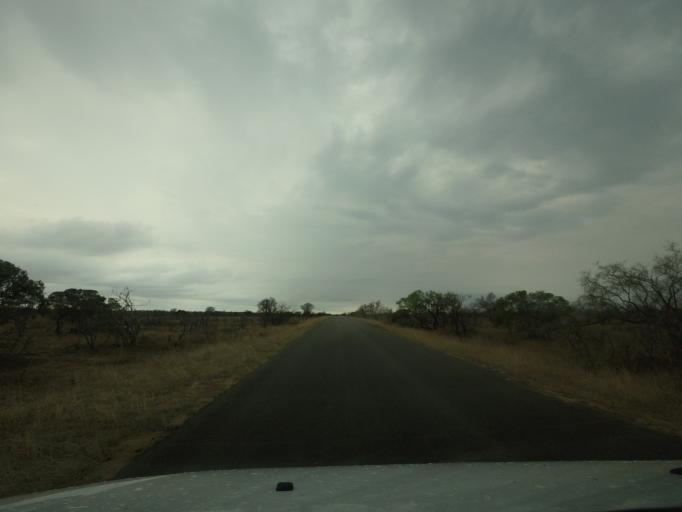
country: ZA
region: Limpopo
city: Thulamahashi
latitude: -24.4686
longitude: 31.4447
